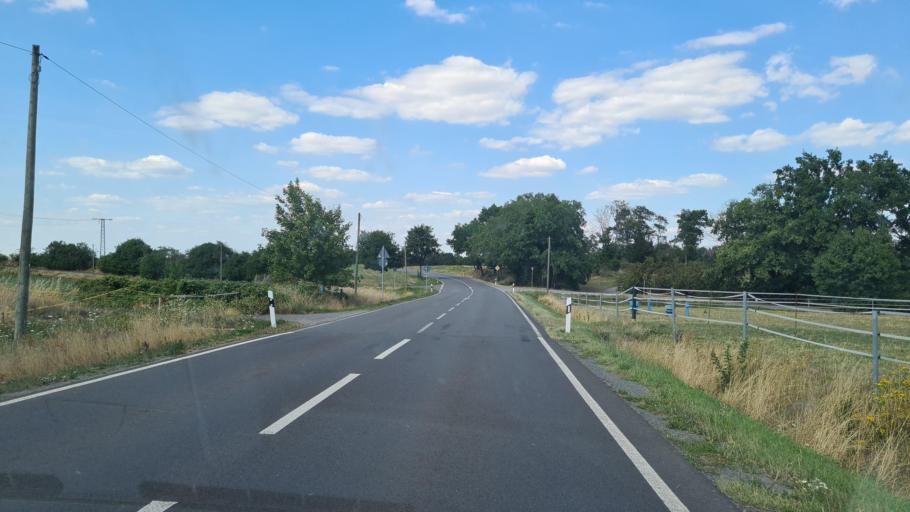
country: DE
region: Saxony
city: Machern
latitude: 51.4022
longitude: 12.6451
